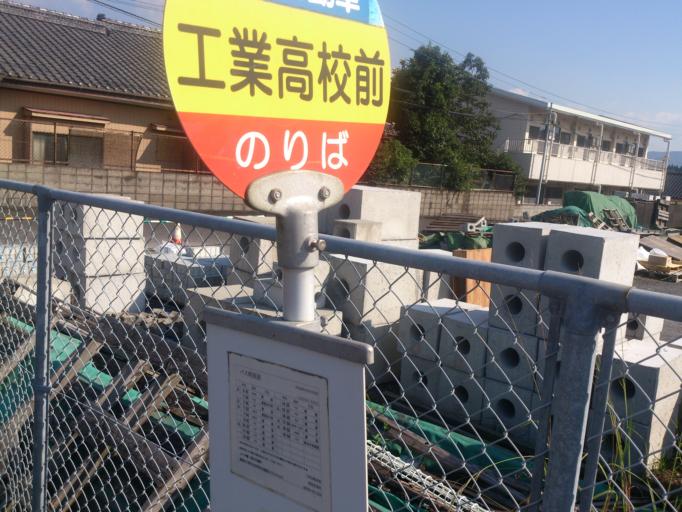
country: JP
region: Kagoshima
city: Kanoya
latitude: 31.3629
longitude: 130.8669
